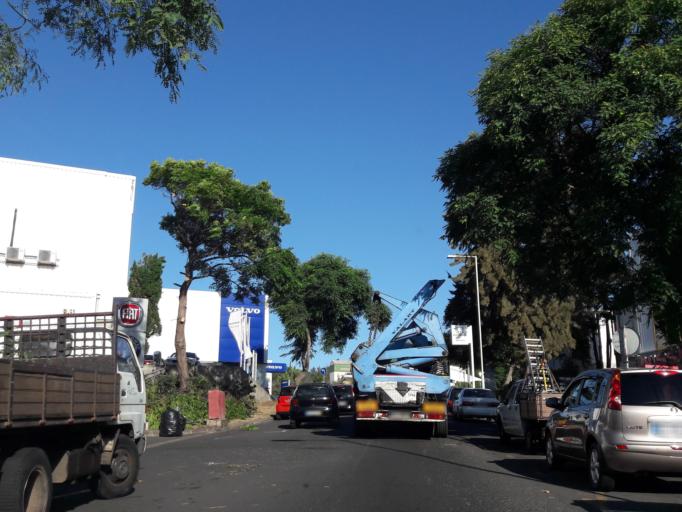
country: PT
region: Madeira
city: Canico
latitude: 32.6503
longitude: -16.8583
